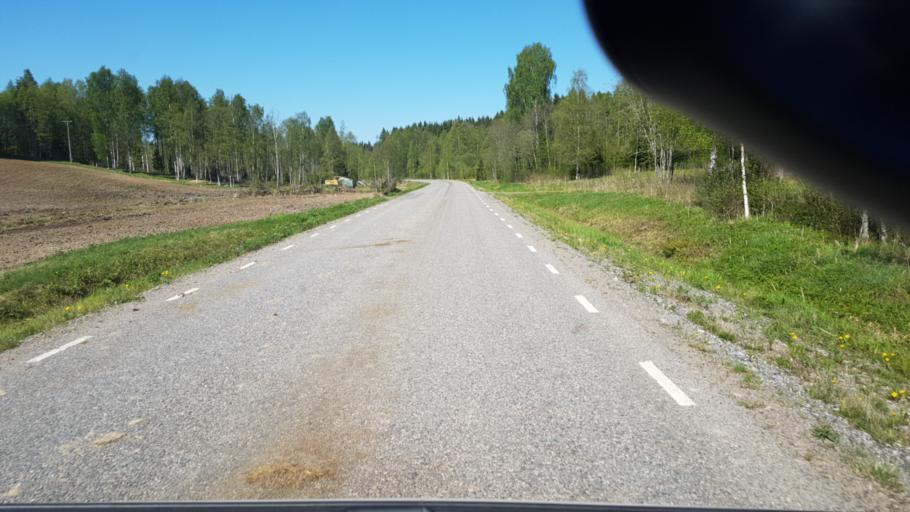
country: SE
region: Vaermland
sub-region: Eda Kommun
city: Charlottenberg
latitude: 59.9894
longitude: 12.3938
